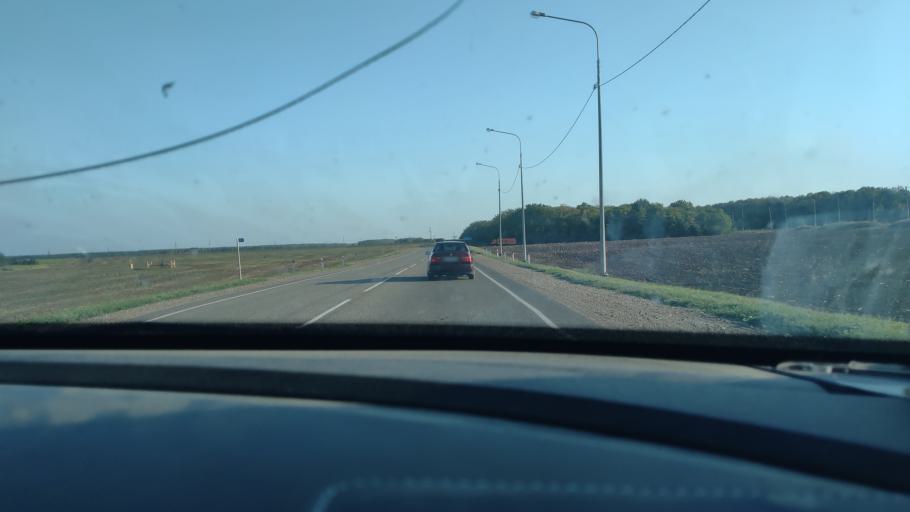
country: RU
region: Krasnodarskiy
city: Novominskaya
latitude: 46.3058
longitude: 38.9309
